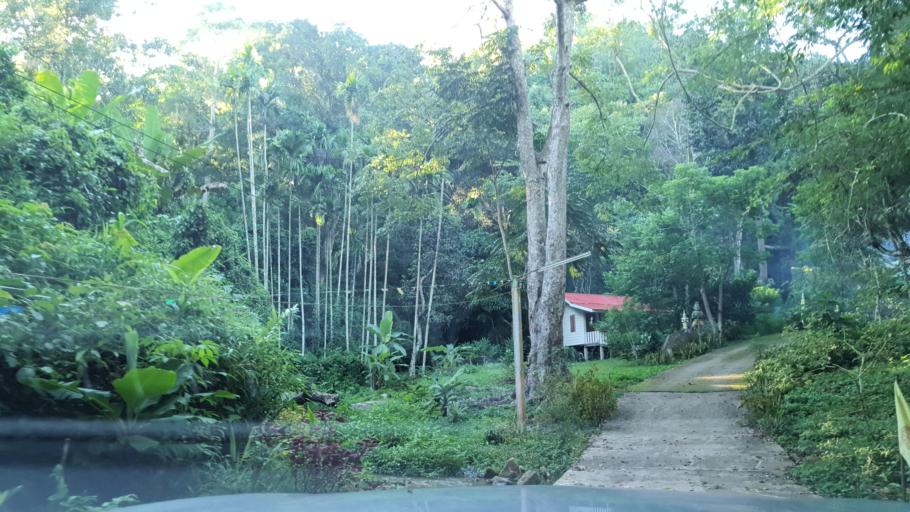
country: TH
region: Chiang Mai
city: Mae On
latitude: 18.8164
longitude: 99.3380
